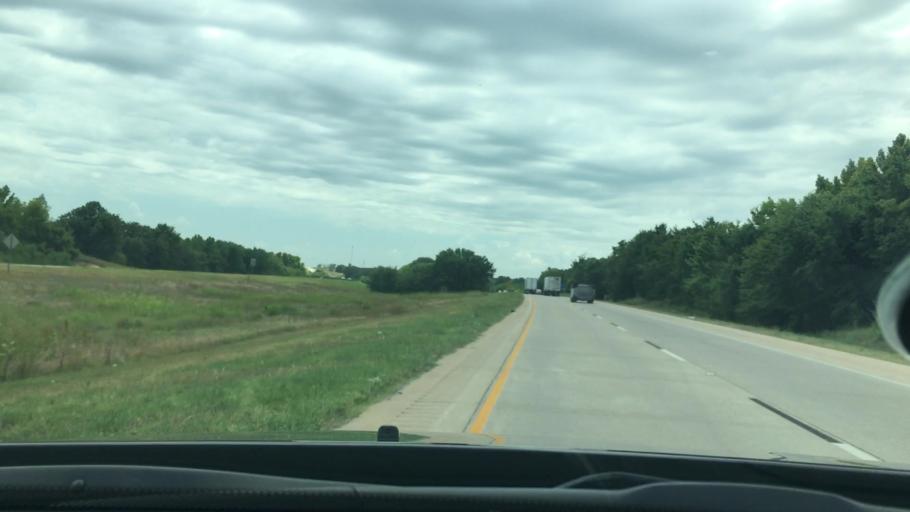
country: US
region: Oklahoma
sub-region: Love County
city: Marietta
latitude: 34.0406
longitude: -97.1503
